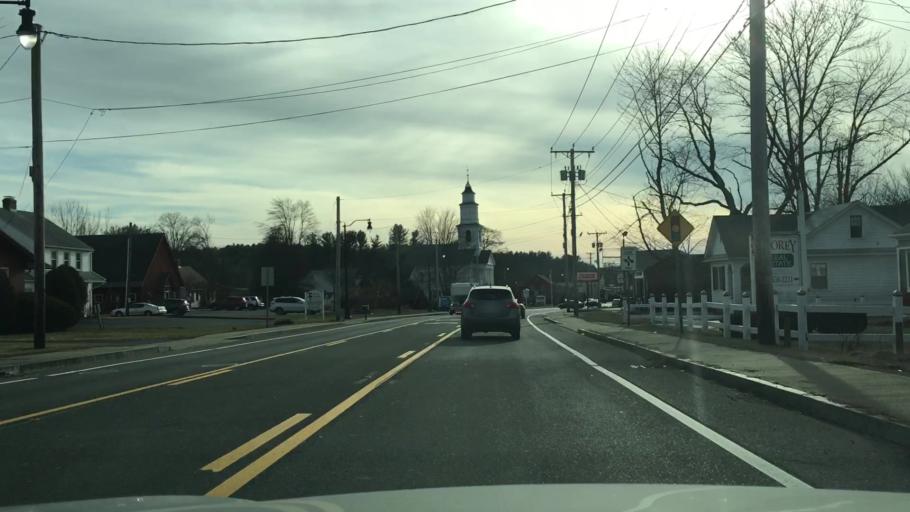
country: US
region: Massachusetts
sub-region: Hampden County
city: Southwick
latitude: 42.0568
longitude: -72.7685
